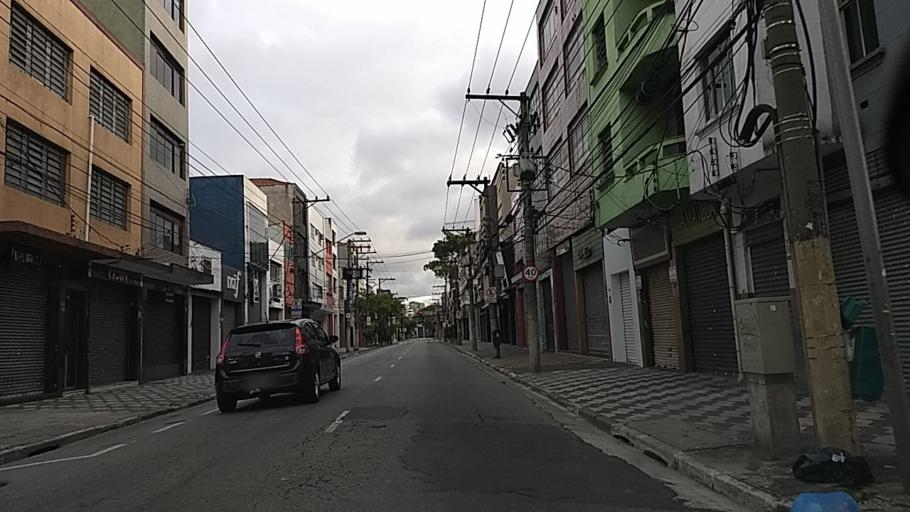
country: BR
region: Sao Paulo
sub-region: Sao Paulo
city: Sao Paulo
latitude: -23.5333
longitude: -46.6139
